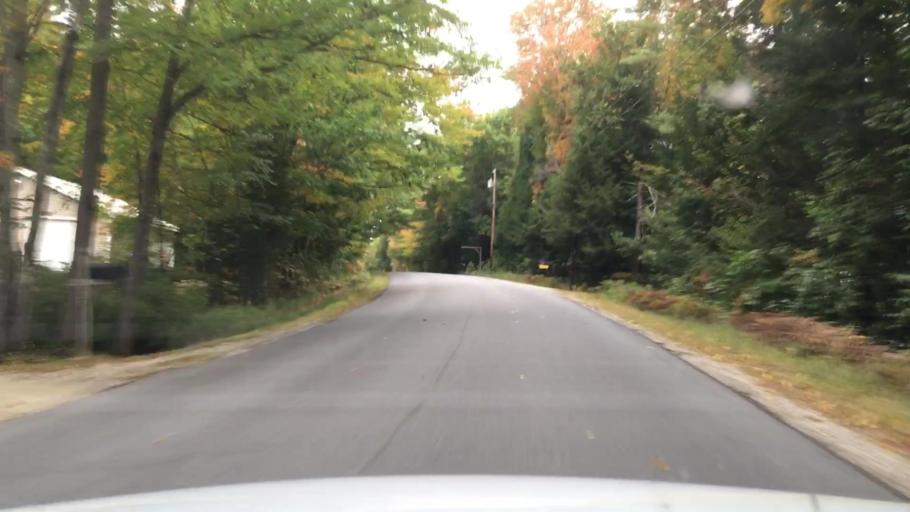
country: US
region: Maine
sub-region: Cumberland County
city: Harrison
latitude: 44.2438
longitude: -70.7189
